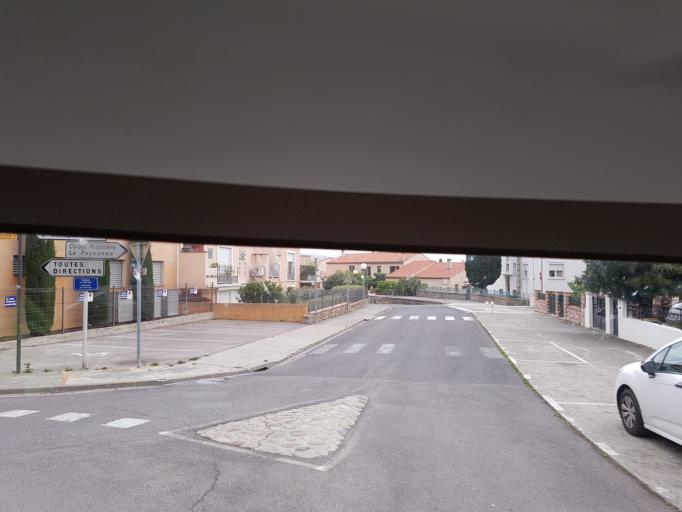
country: FR
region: Languedoc-Roussillon
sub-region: Departement des Pyrenees-Orientales
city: Prades
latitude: 42.6207
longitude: 2.4268
